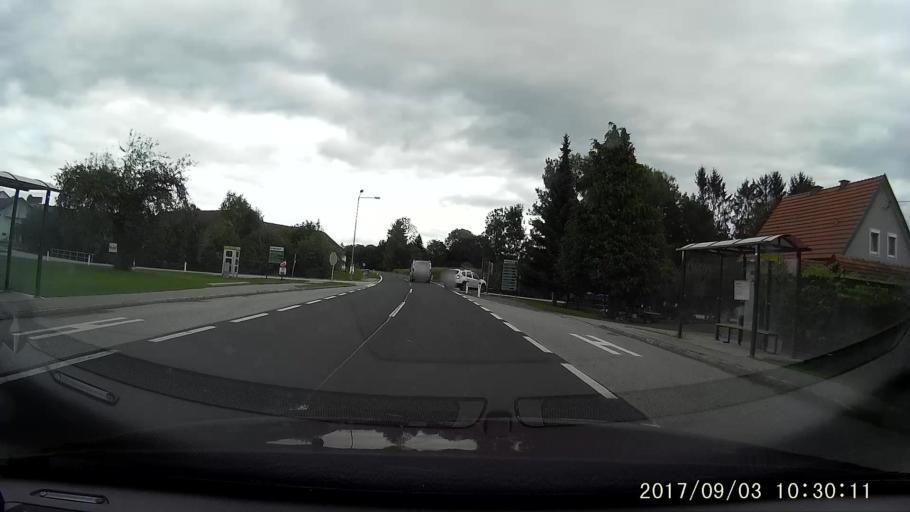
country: AT
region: Styria
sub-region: Politischer Bezirk Hartberg-Fuerstenfeld
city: Ilz
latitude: 47.0834
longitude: 15.9429
